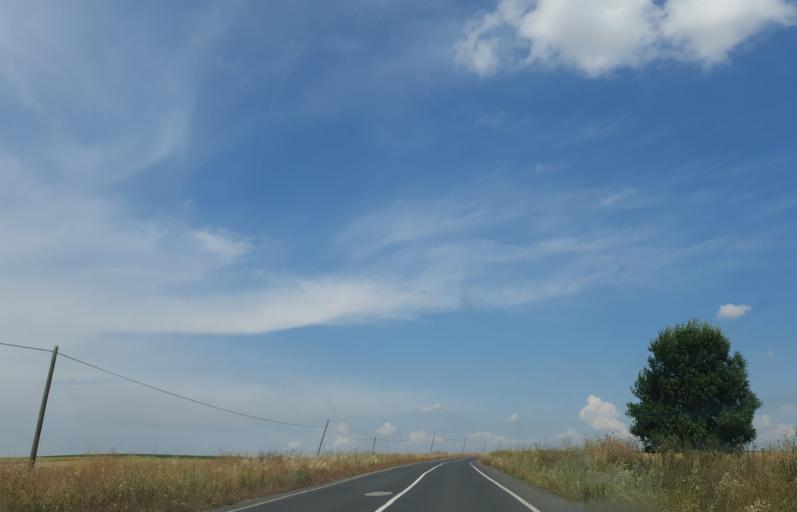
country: TR
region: Kirklareli
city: Buyukkaristiran
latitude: 41.2451
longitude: 27.6047
